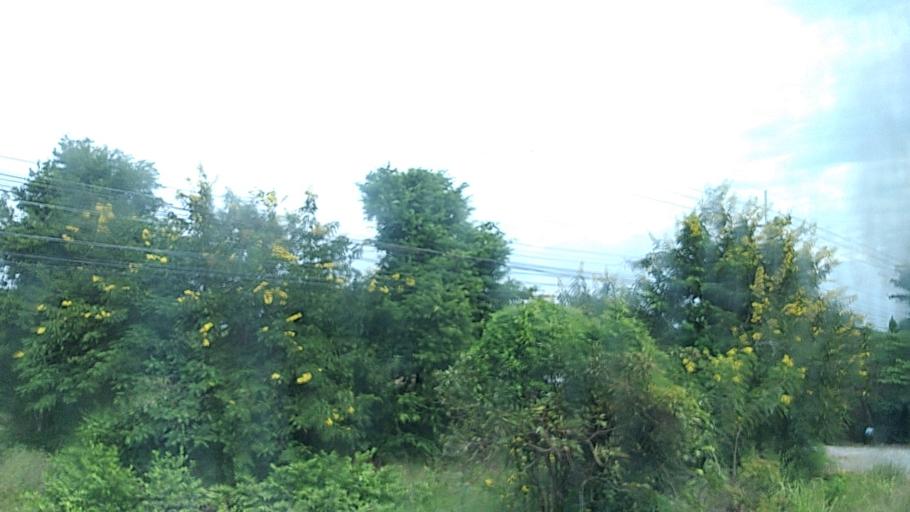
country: TH
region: Maha Sarakham
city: Maha Sarakham
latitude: 16.1591
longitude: 103.3602
